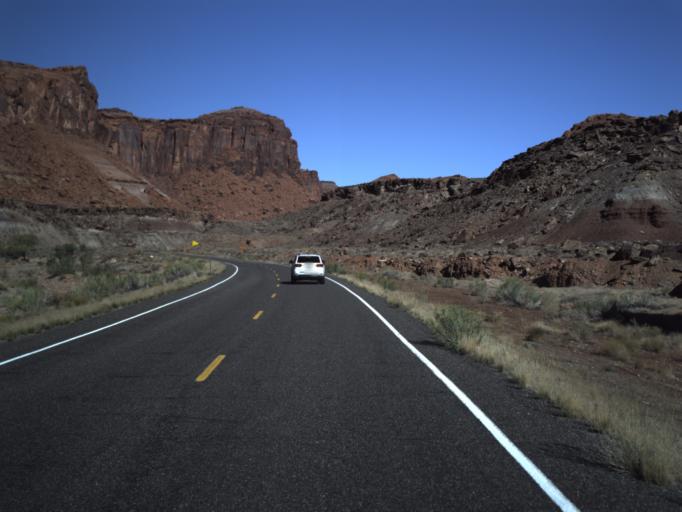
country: US
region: Utah
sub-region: San Juan County
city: Blanding
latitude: 37.9148
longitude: -110.4599
